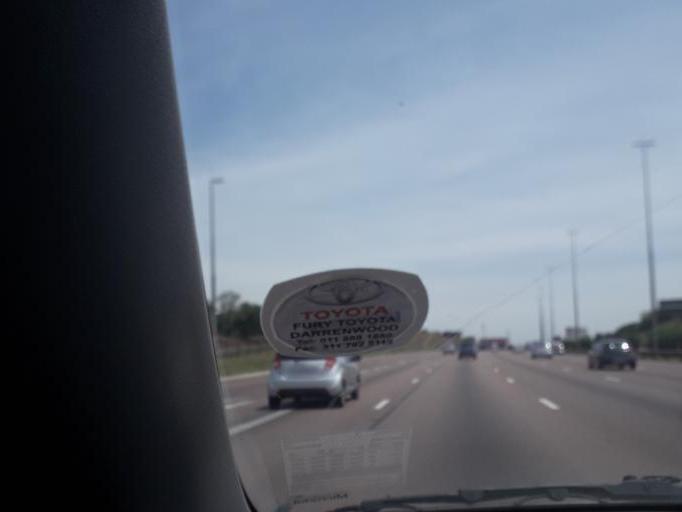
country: ZA
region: Gauteng
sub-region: City of Tshwane Metropolitan Municipality
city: Centurion
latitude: -25.8121
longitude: 28.2577
